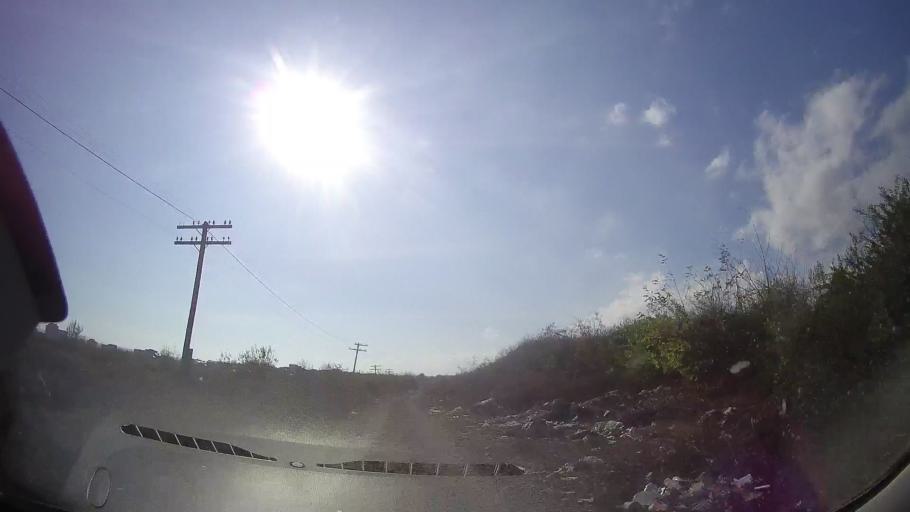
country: RO
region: Constanta
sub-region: Comuna Costinesti
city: Costinesti
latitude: 43.9688
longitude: 28.6419
